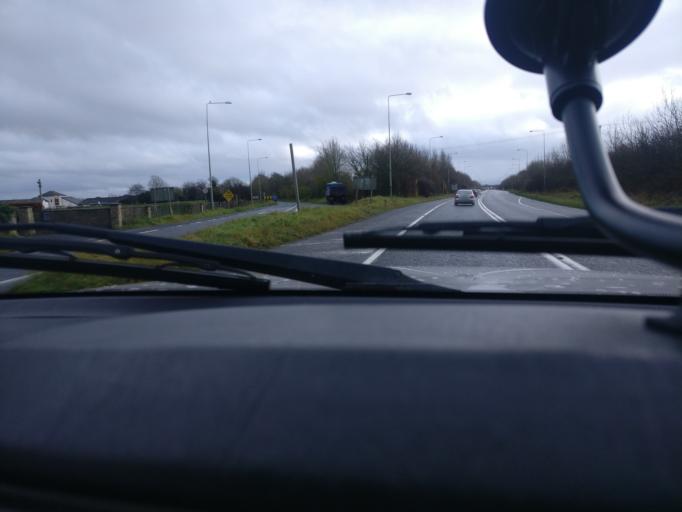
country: IE
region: Leinster
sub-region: Kildare
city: Kilcock
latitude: 53.4097
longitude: -6.7036
